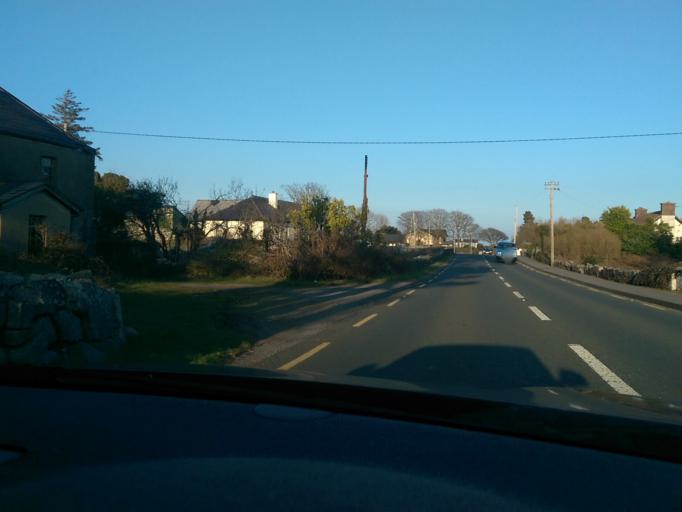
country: IE
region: Connaught
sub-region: County Galway
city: Oughterard
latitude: 53.2459
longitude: -9.3778
